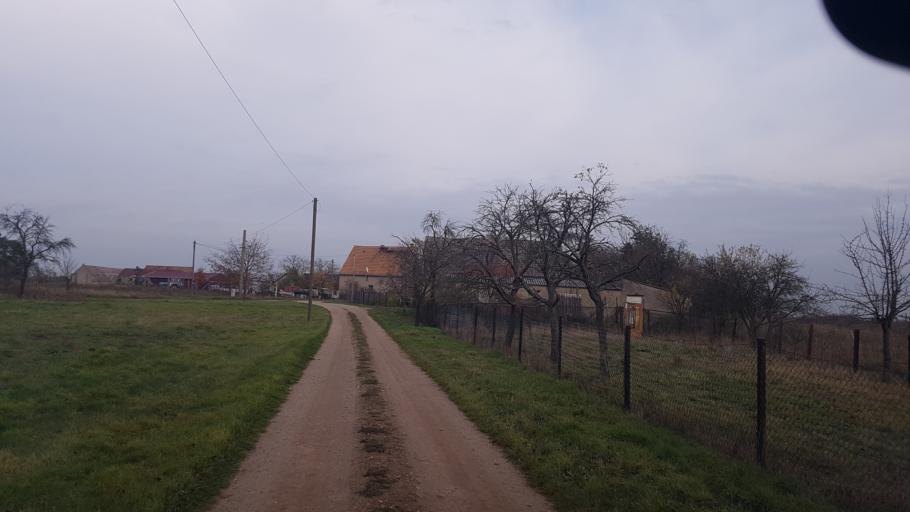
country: DE
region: Brandenburg
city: Schilda
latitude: 51.6604
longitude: 13.4079
